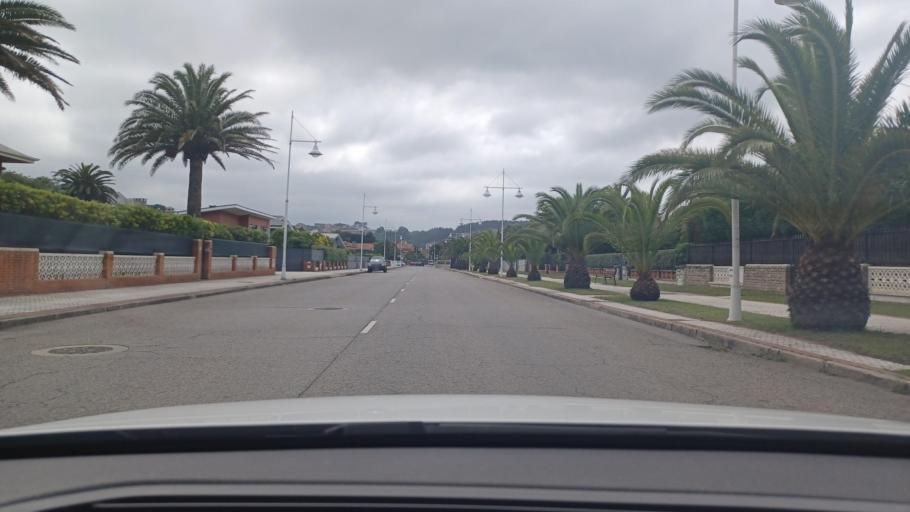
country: ES
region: Asturias
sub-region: Province of Asturias
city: Aviles
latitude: 43.5781
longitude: -5.9524
